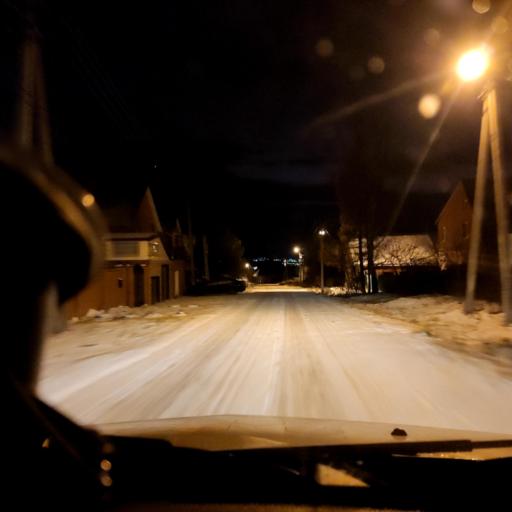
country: RU
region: Bashkortostan
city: Mikhaylovka
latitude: 54.8307
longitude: 55.9079
